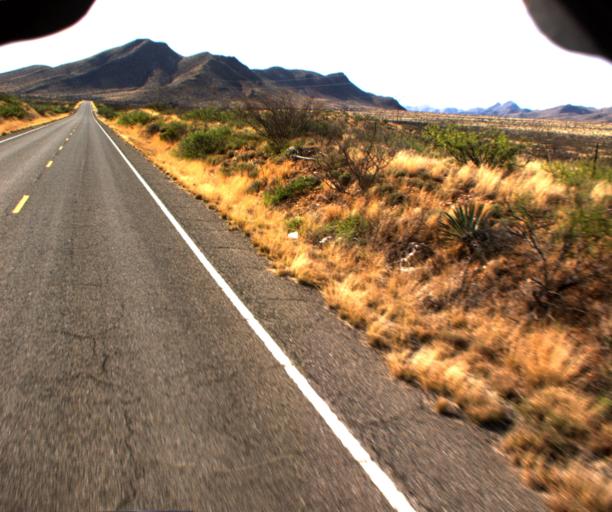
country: US
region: Arizona
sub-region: Cochise County
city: Willcox
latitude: 32.1800
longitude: -109.6341
